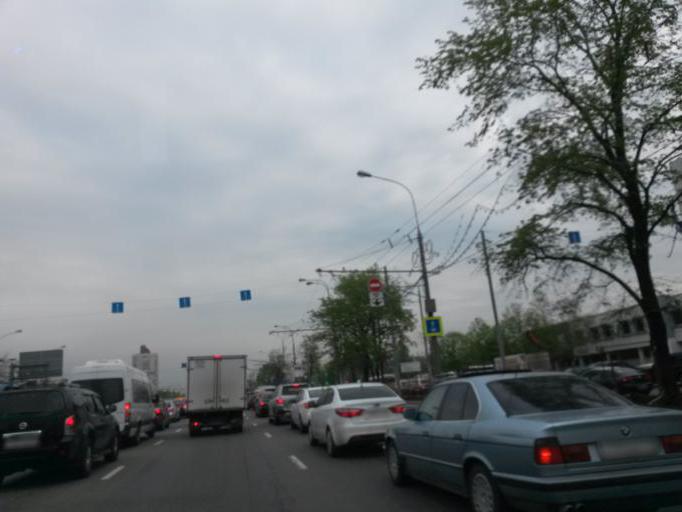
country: RU
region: Moscow
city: Orekhovo-Borisovo
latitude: 55.6001
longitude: 37.7235
